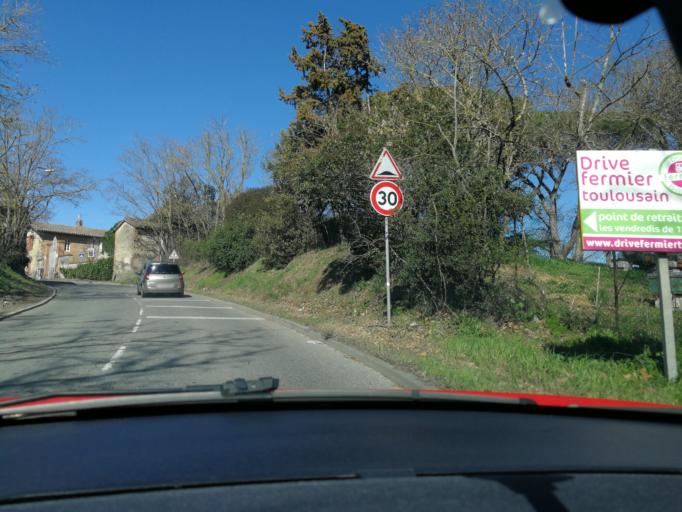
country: FR
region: Midi-Pyrenees
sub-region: Departement de la Haute-Garonne
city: Portet-sur-Garonne
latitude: 43.5431
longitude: 1.3893
